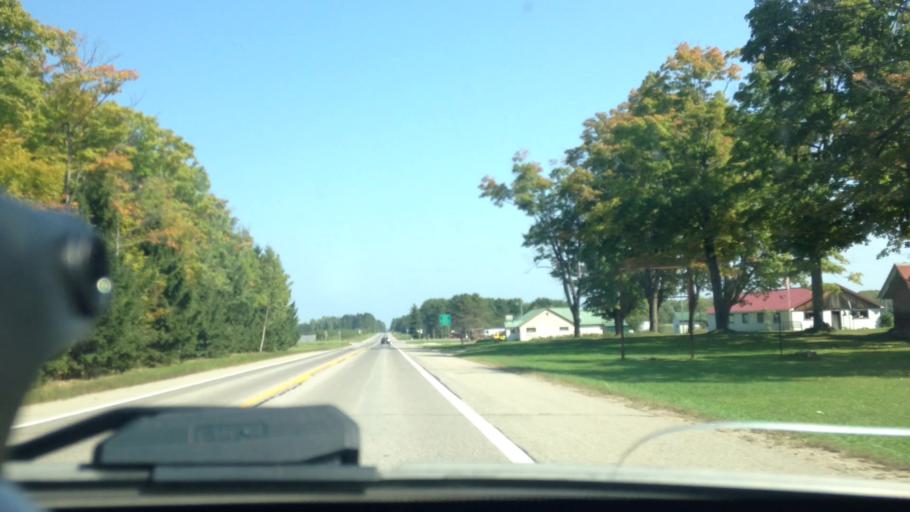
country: US
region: Michigan
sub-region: Luce County
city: Newberry
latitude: 46.3035
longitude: -85.4610
